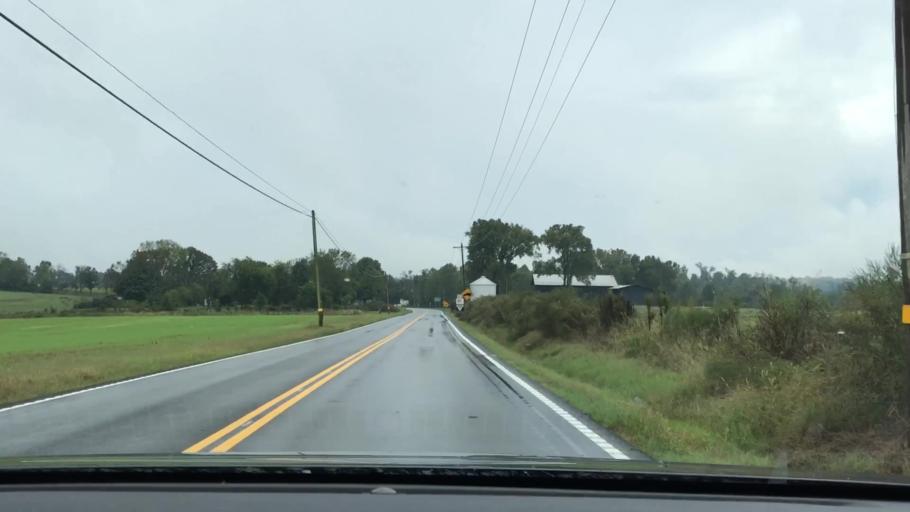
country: US
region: Tennessee
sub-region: Macon County
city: Red Boiling Springs
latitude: 36.4519
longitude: -85.8808
